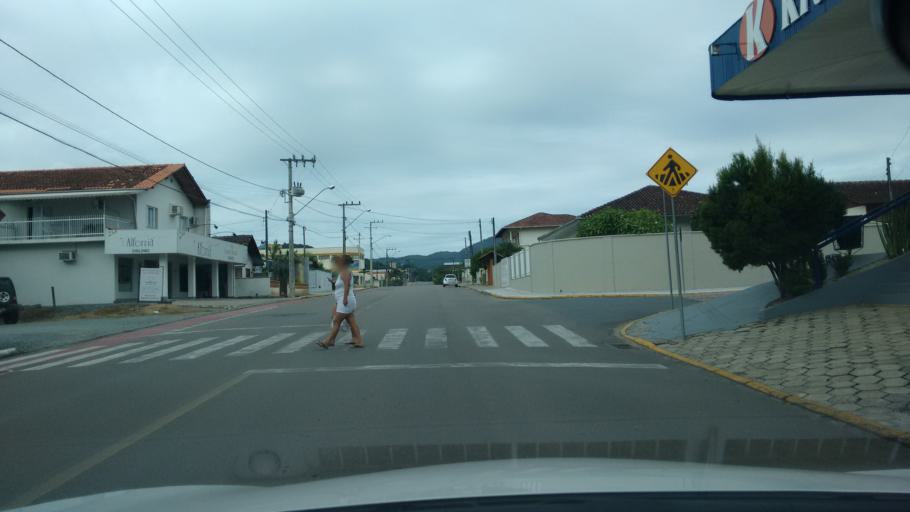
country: BR
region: Santa Catarina
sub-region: Timbo
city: Timbo
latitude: -26.8124
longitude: -49.2718
